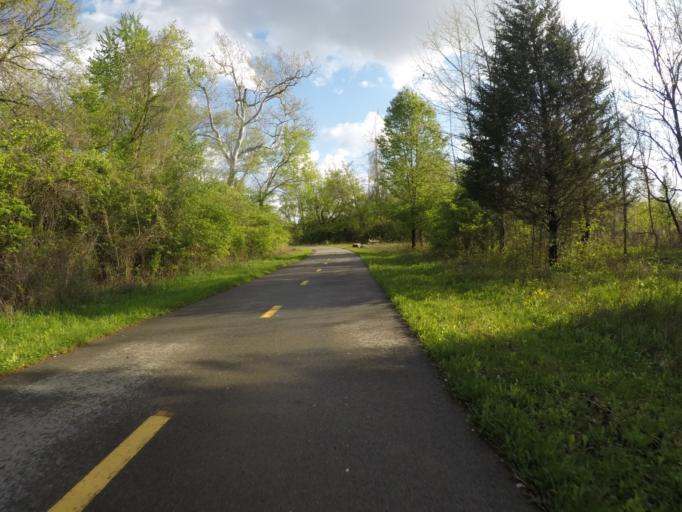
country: US
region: Ohio
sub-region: Franklin County
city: Bexley
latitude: 39.9917
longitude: -82.9383
